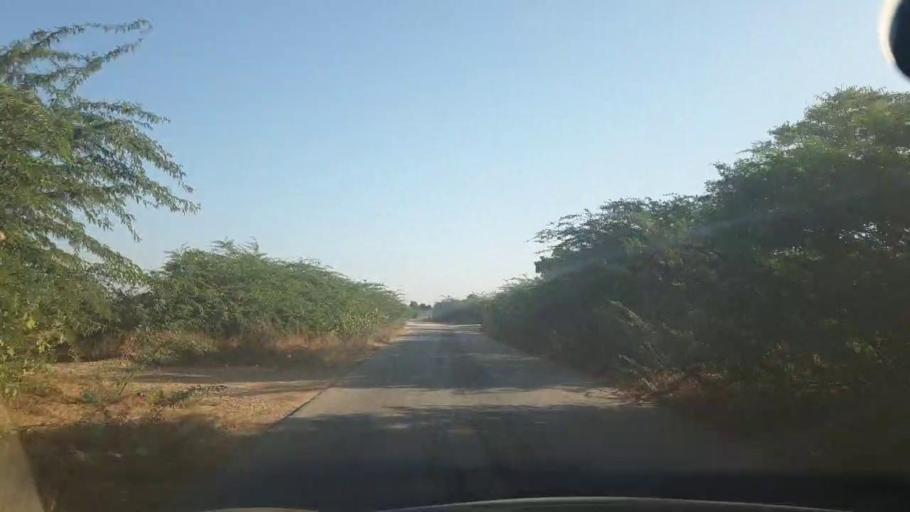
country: PK
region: Sindh
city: Malir Cantonment
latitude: 25.1072
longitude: 67.2619
